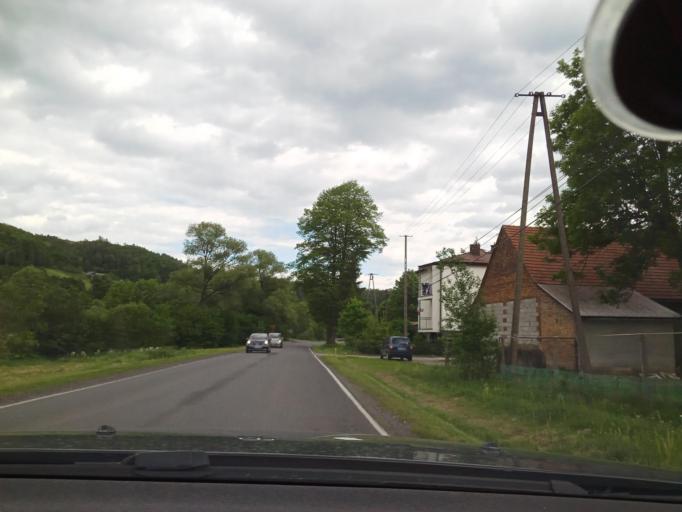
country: PL
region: Lesser Poland Voivodeship
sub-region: Powiat limanowski
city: Tymbark
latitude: 49.7500
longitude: 20.3605
